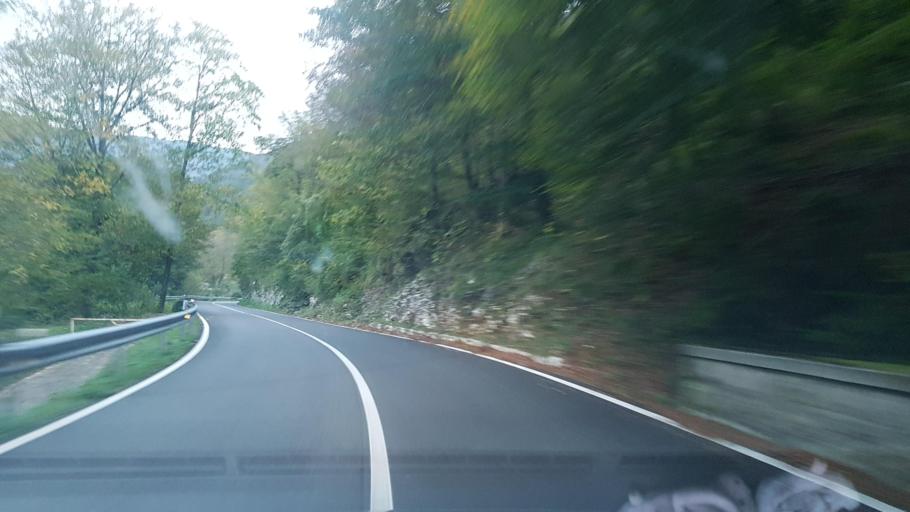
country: IT
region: Friuli Venezia Giulia
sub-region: Provincia di Pordenone
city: Anduins
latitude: 46.2617
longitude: 12.9566
